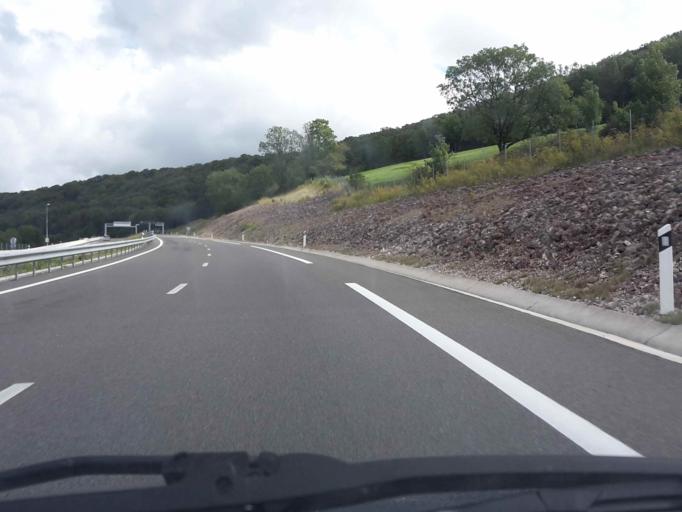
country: FR
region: Franche-Comte
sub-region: Departement du Doubs
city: Beure
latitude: 47.2092
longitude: 6.0357
